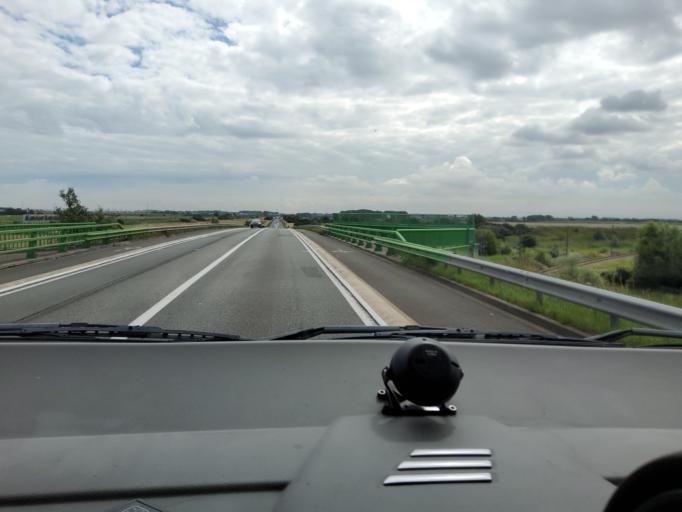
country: FR
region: Nord-Pas-de-Calais
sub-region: Departement du Nord
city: Gravelines
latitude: 50.9959
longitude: 2.1666
